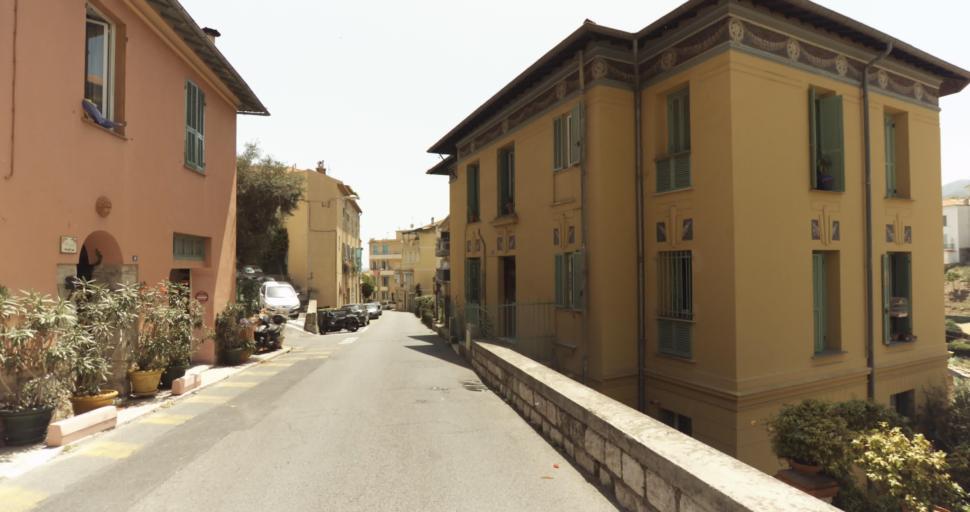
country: FR
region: Provence-Alpes-Cote d'Azur
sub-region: Departement des Alpes-Maritimes
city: Menton
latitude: 43.7782
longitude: 7.5044
